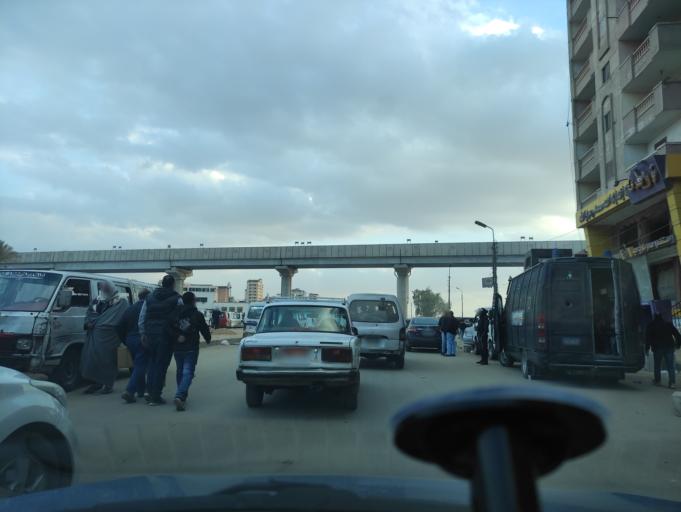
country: EG
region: Muhafazat al Qalyubiyah
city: Al Khankah
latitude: 30.1293
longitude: 31.3614
